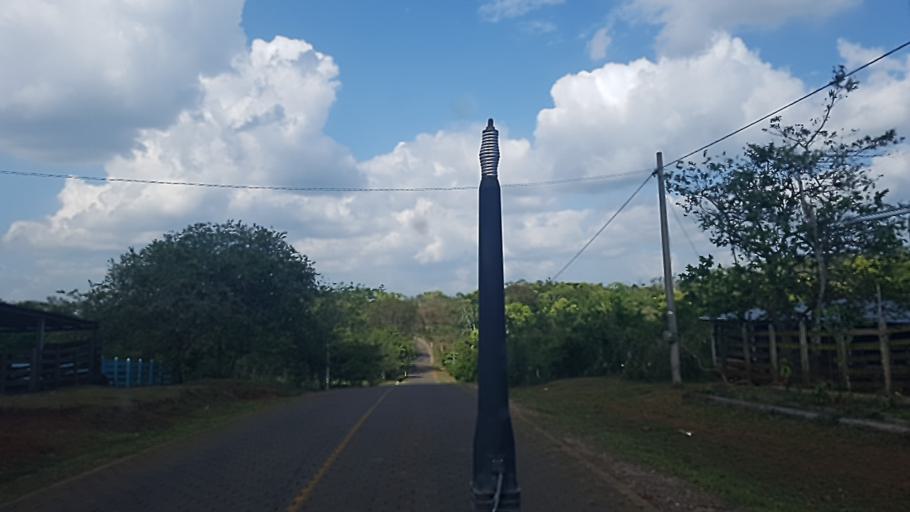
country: NI
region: Atlantico Sur
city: Nueva Guinea
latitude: 11.6974
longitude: -84.3890
